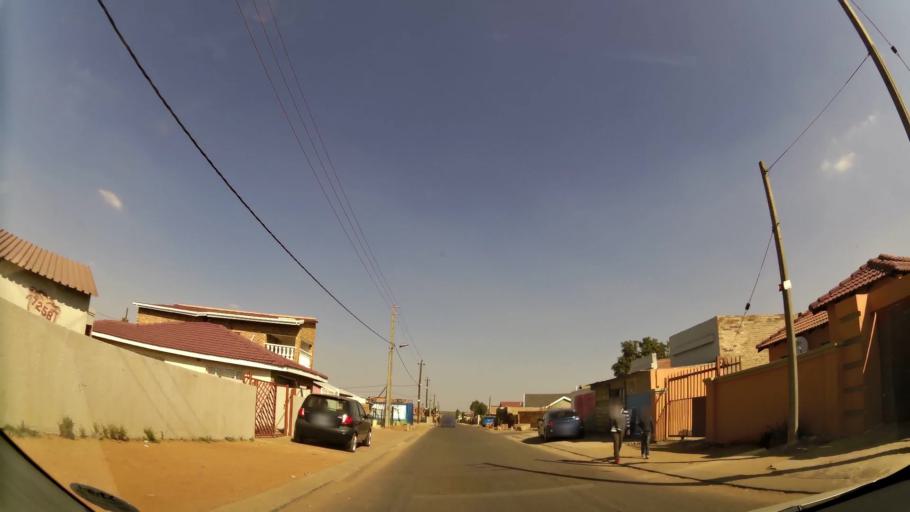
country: ZA
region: Gauteng
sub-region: City of Johannesburg Metropolitan Municipality
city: Roodepoort
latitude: -26.1613
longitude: 27.7979
